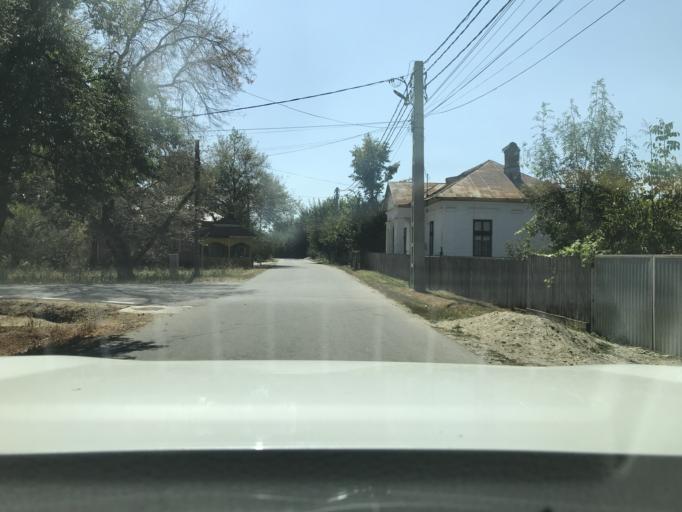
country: RO
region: Olt
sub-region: Comuna Falcoiu
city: Falcoiu
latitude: 44.2429
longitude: 24.3665
